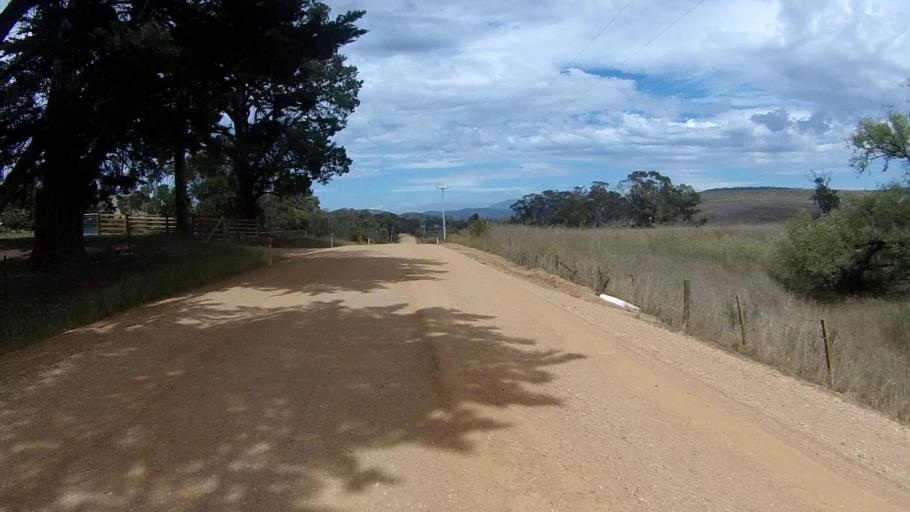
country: AU
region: Tasmania
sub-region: Sorell
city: Sorell
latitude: -42.6924
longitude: 147.4655
